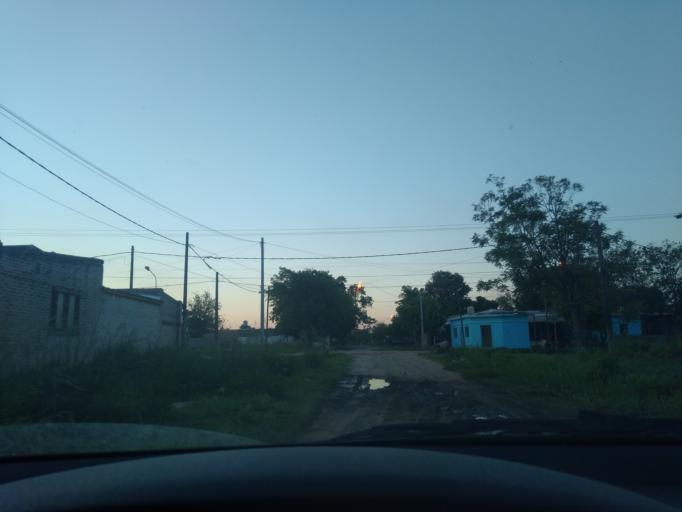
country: AR
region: Chaco
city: Barranqueras
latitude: -27.4768
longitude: -58.9339
